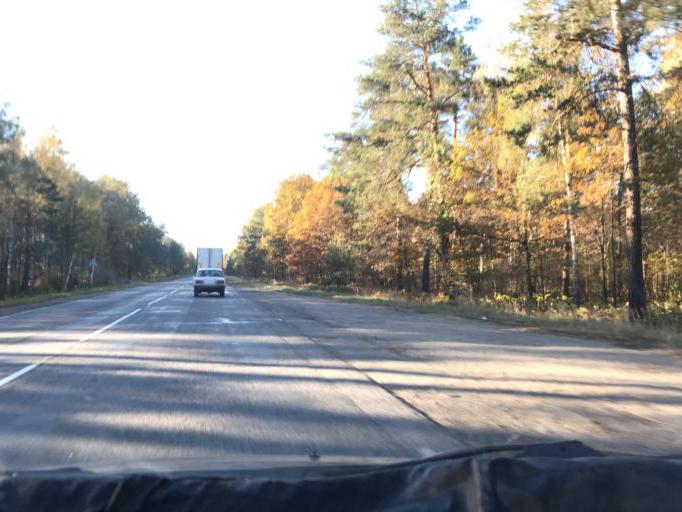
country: BY
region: Gomel
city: Mazyr
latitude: 52.2031
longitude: 29.0762
